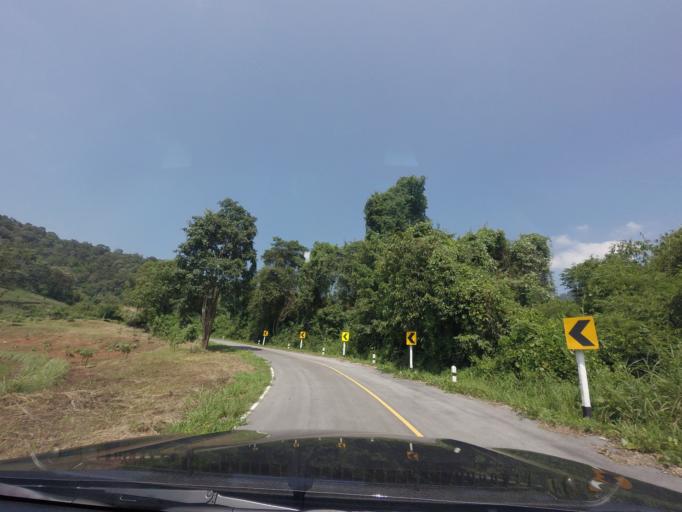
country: TH
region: Loei
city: Na Haeo
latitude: 17.5661
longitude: 100.9841
